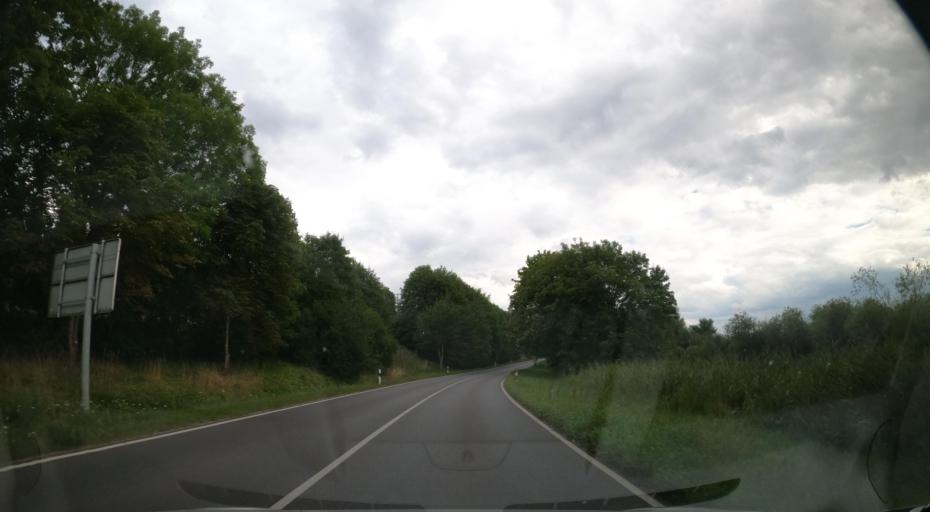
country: DE
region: Mecklenburg-Vorpommern
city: Woldegk
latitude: 53.4626
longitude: 13.6017
